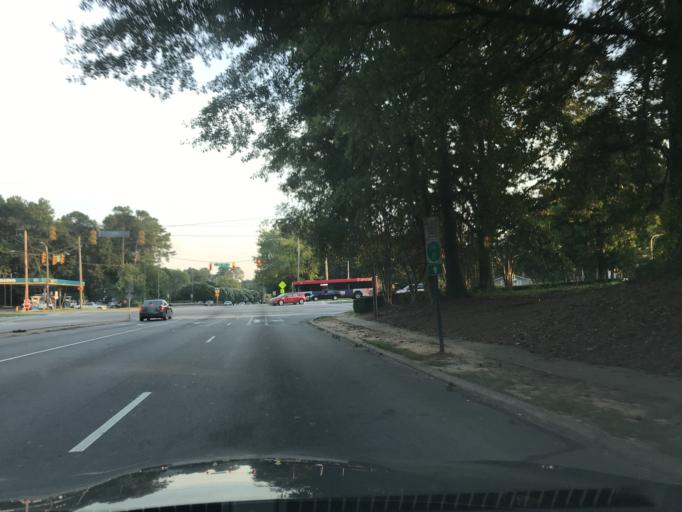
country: US
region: North Carolina
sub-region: Wake County
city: Raleigh
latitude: 35.7806
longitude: -78.6135
